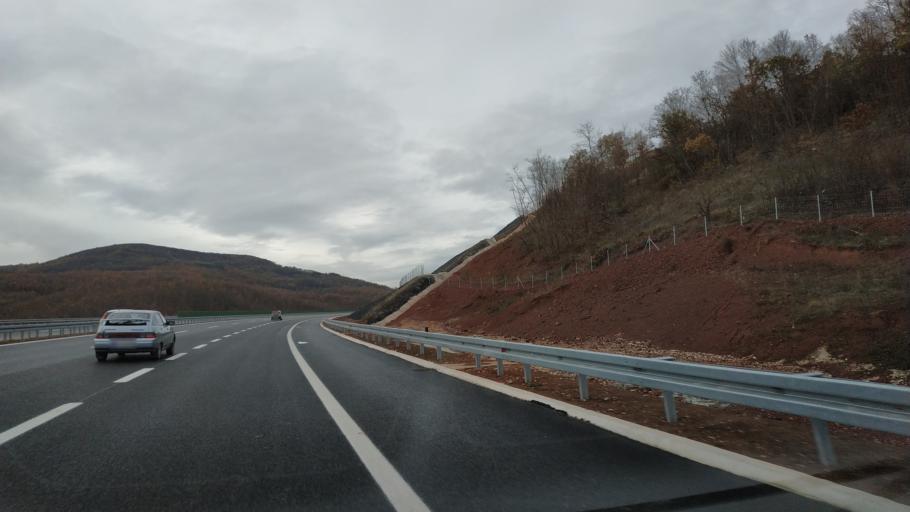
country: RS
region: Central Serbia
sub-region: Nisavski Okrug
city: Gadzin Han
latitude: 43.2578
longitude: 22.1506
